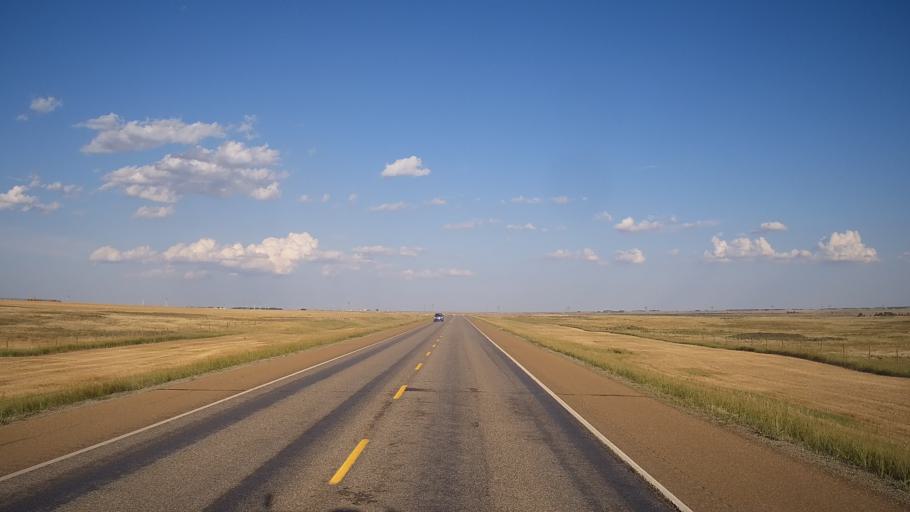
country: CA
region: Alberta
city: Hanna
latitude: 51.6238
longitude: -111.8770
